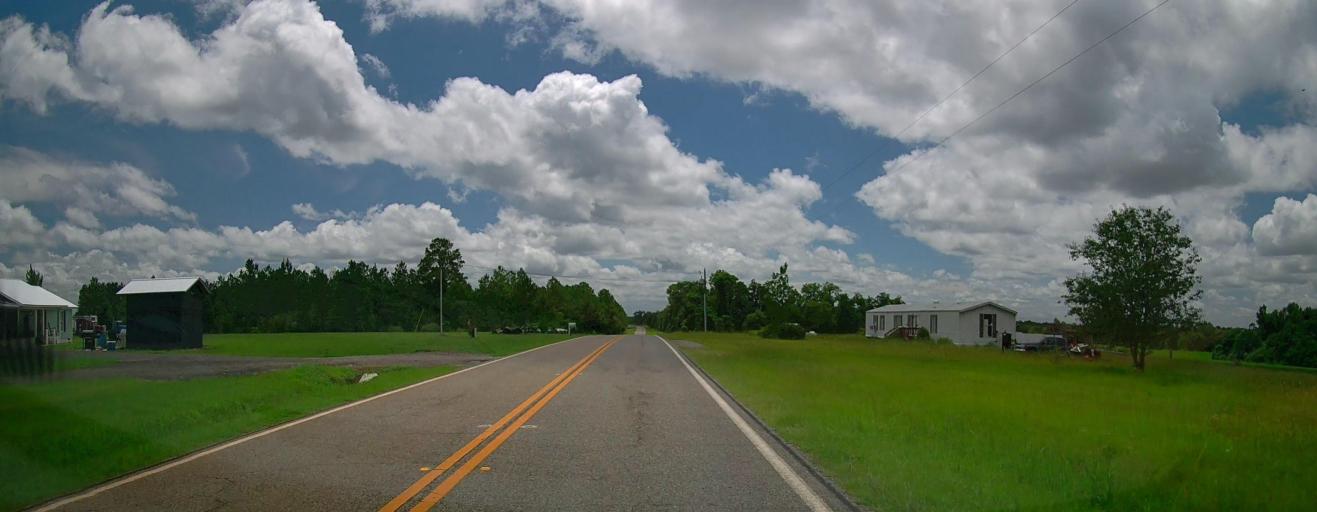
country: US
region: Georgia
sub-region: Wilcox County
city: Rochelle
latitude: 31.8905
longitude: -83.5543
